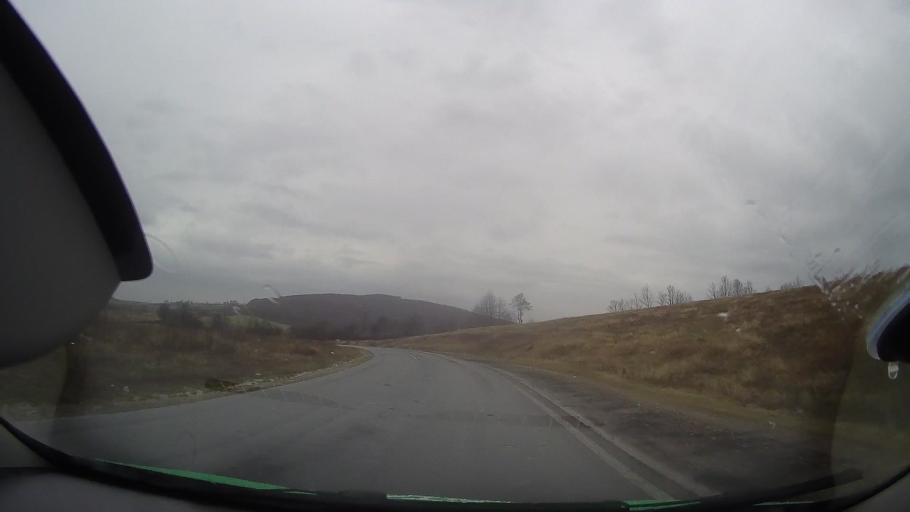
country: RO
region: Bihor
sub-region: Comuna Rabagani
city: Rabagani
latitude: 46.7275
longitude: 22.2401
